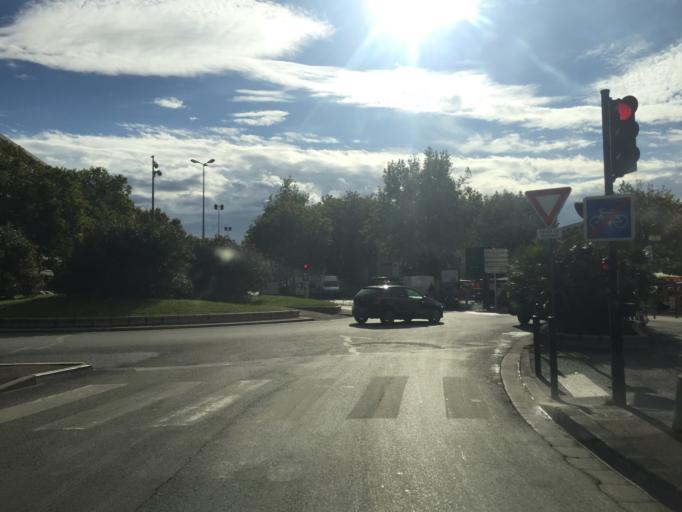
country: FR
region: Provence-Alpes-Cote d'Azur
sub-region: Departement des Bouches-du-Rhone
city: Aix-en-Provence
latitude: 43.5241
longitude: 5.4329
